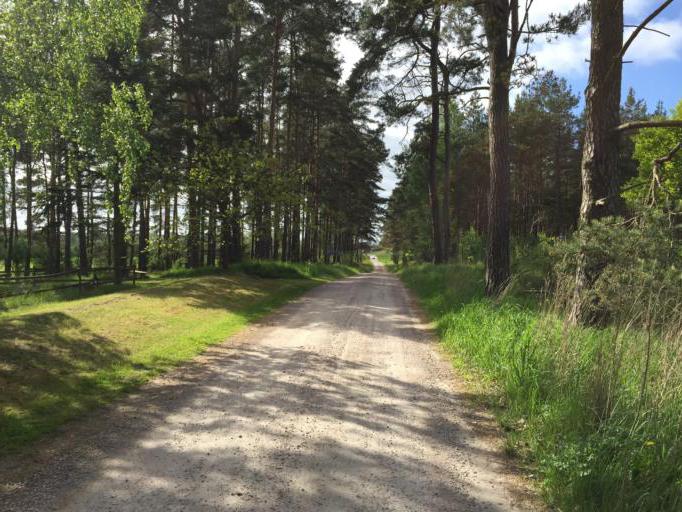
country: SE
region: Skane
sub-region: Sjobo Kommun
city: Sjoebo
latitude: 55.6672
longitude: 13.6312
